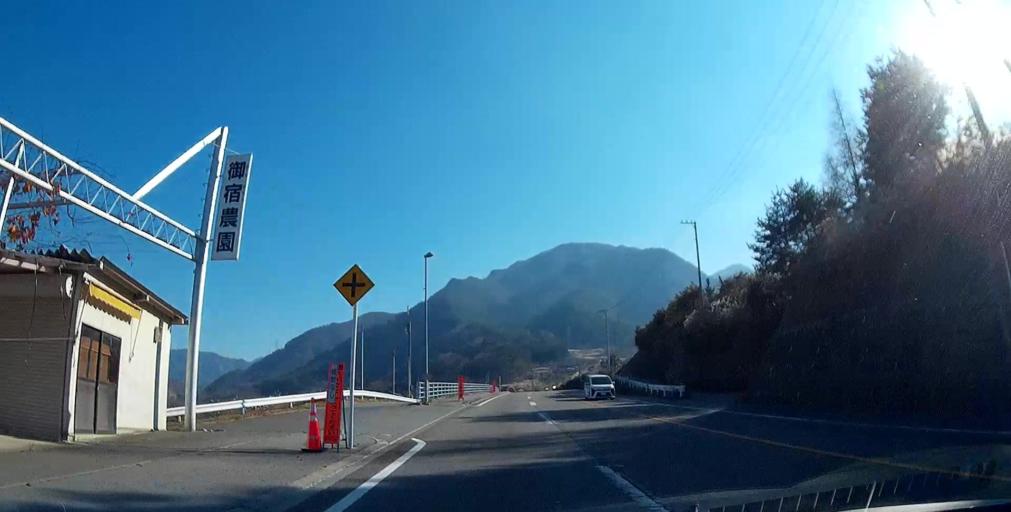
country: JP
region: Yamanashi
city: Isawa
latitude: 35.5974
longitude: 138.7117
